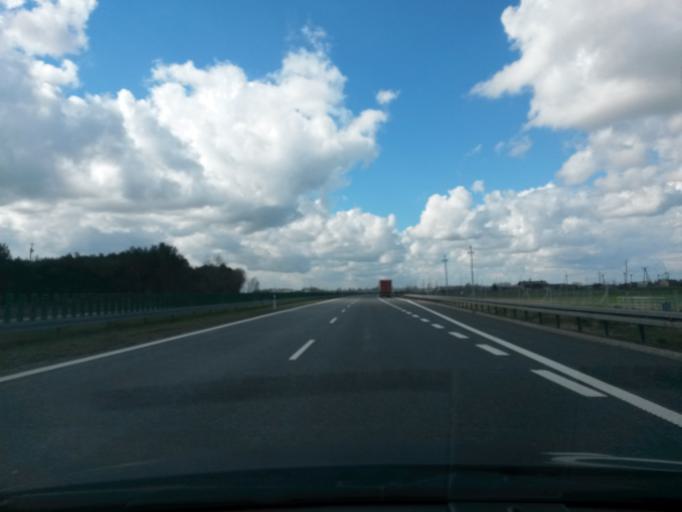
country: PL
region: Lodz Voivodeship
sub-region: Powiat leczycki
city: Swinice Warckie
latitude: 52.0333
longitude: 18.8836
